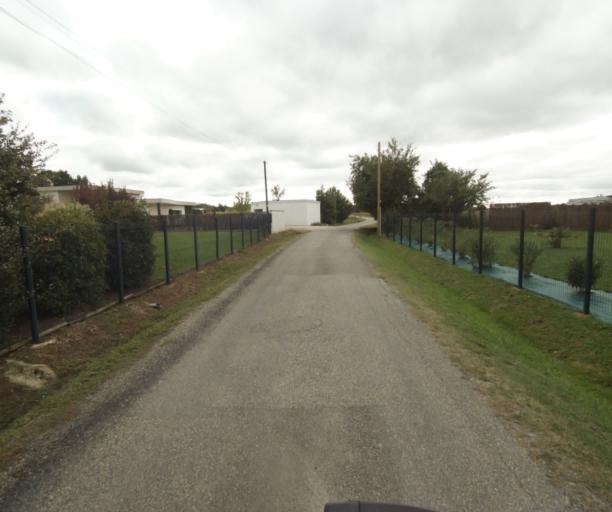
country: FR
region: Midi-Pyrenees
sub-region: Departement du Tarn-et-Garonne
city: Montech
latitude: 43.9632
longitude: 1.2535
